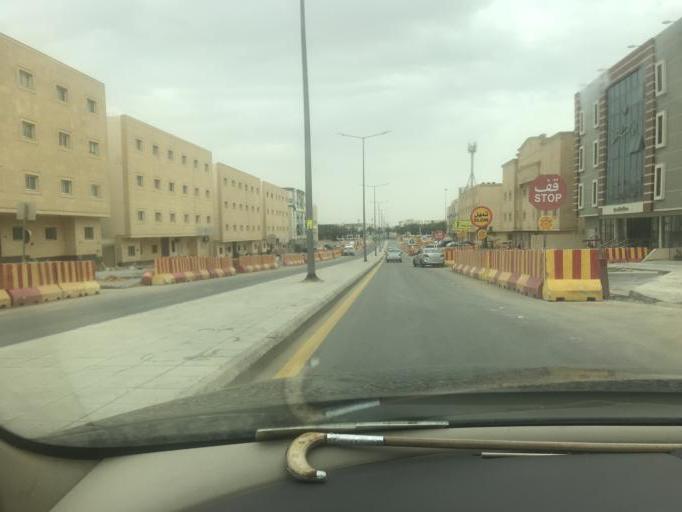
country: SA
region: Ar Riyad
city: Riyadh
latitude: 24.7912
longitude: 46.7109
